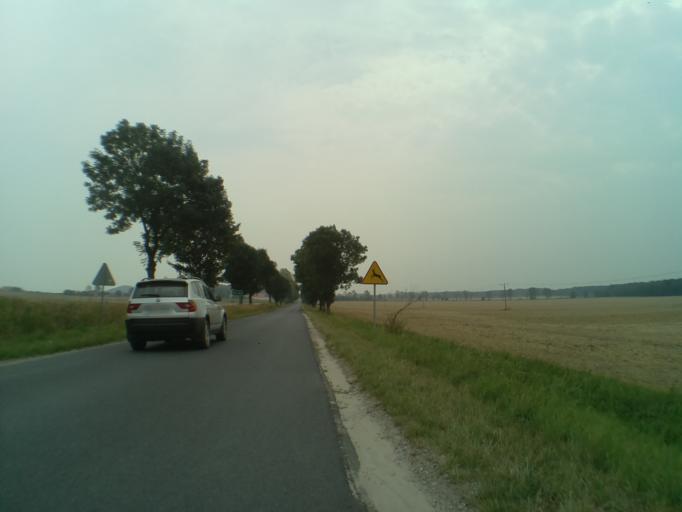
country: PL
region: Lower Silesian Voivodeship
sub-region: Powiat swidnicki
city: Strzegom
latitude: 50.9810
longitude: 16.2735
